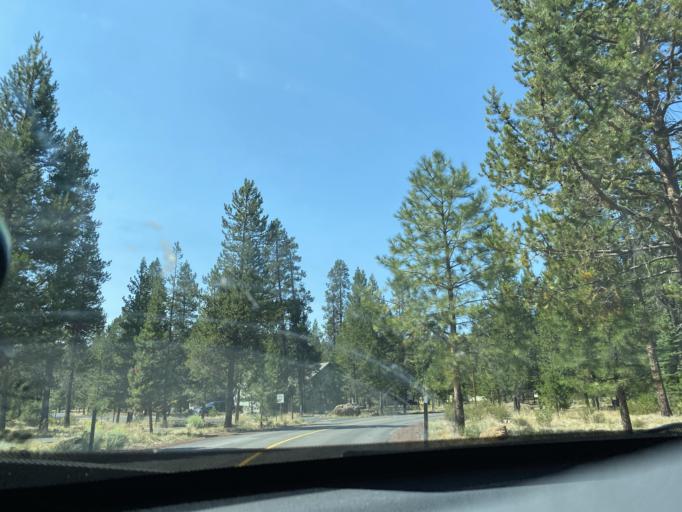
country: US
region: Oregon
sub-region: Deschutes County
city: Sunriver
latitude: 43.8927
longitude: -121.4190
